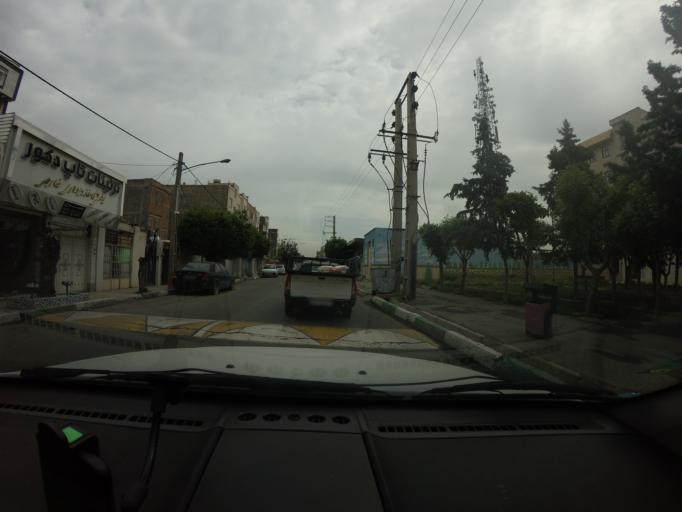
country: IR
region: Tehran
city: Eslamshahr
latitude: 35.5426
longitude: 51.2339
